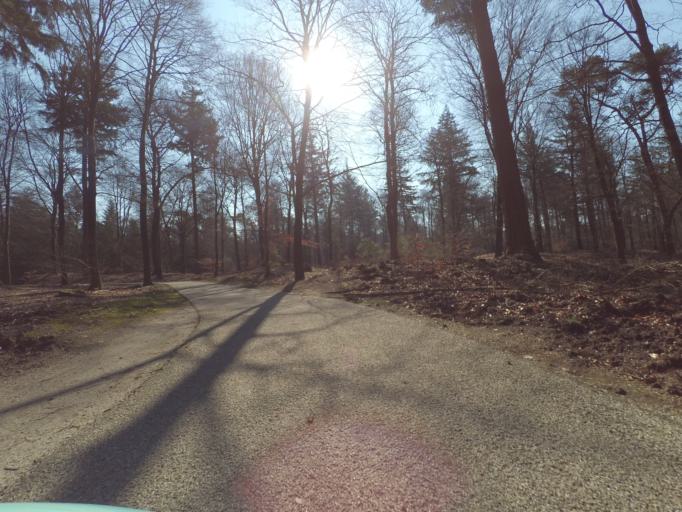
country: NL
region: Gelderland
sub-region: Gemeente Ede
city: Otterlo
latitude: 52.1212
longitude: 5.8358
